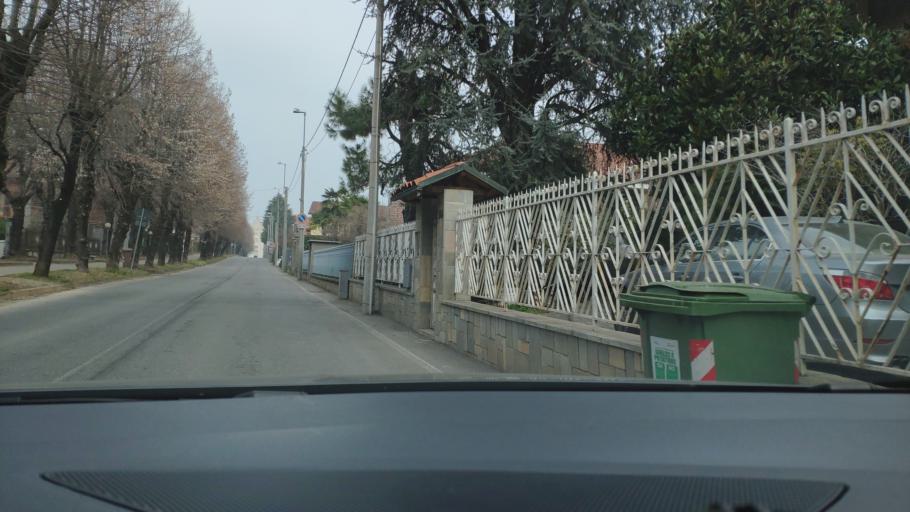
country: IT
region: Piedmont
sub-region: Provincia di Torino
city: Pianezza
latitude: 45.1100
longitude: 7.5456
